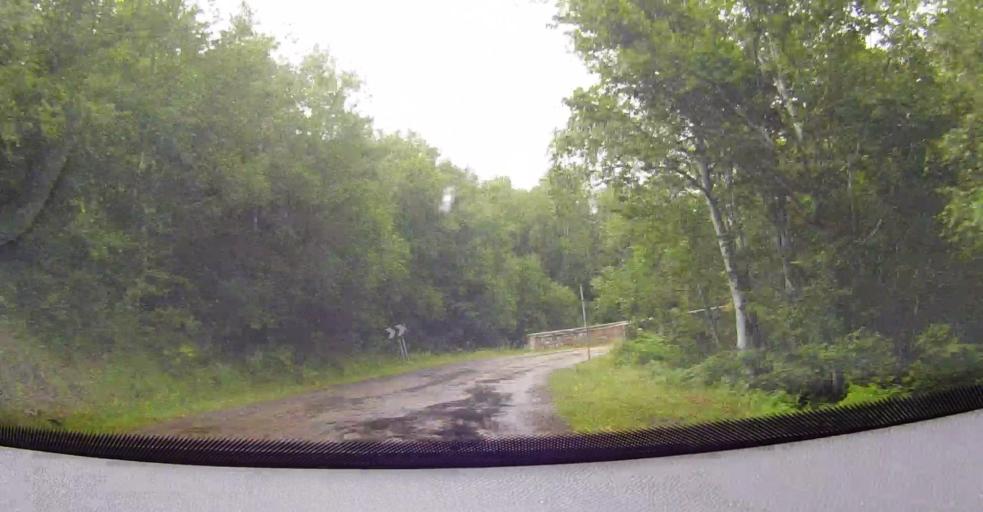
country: ES
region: Castille and Leon
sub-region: Provincia de Leon
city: Puebla de Lillo
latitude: 43.0726
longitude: -5.2667
